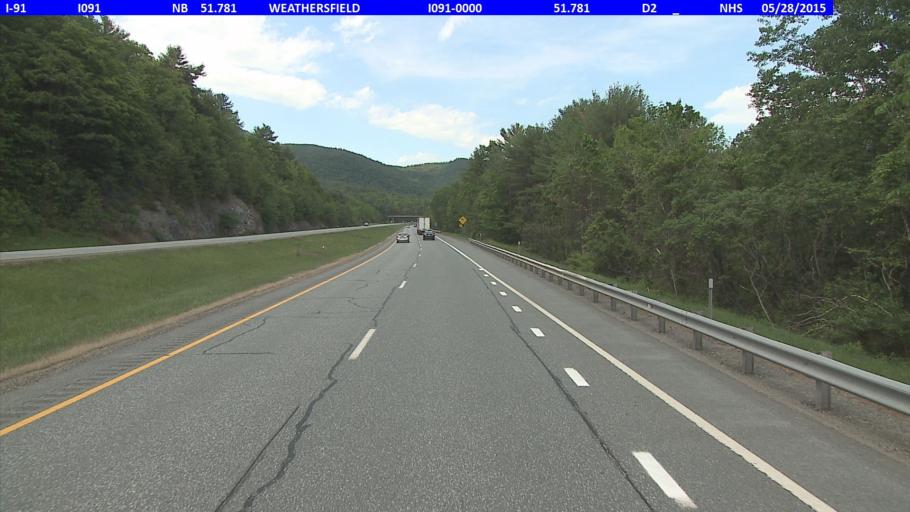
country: US
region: New Hampshire
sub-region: Sullivan County
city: Claremont
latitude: 43.4088
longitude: -72.4141
